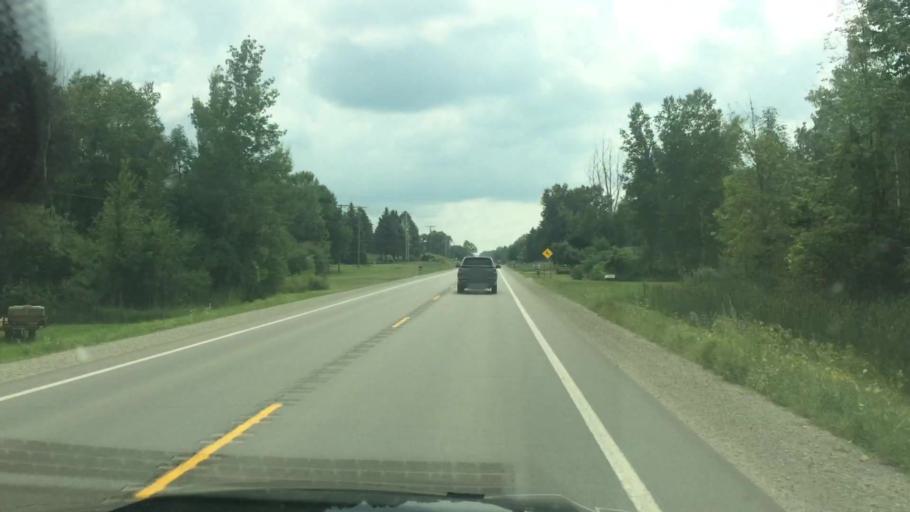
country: US
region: Michigan
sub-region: Tuscola County
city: Cass City
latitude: 43.5782
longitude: -83.0966
